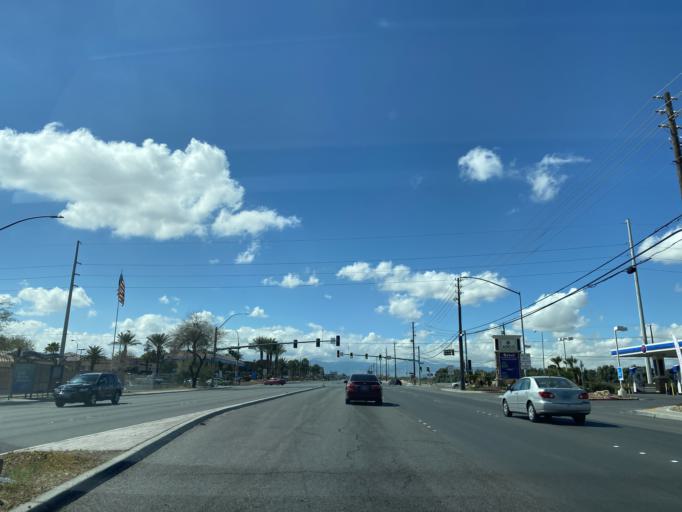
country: US
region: Nevada
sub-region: Clark County
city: North Las Vegas
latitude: 36.2396
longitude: -115.1424
